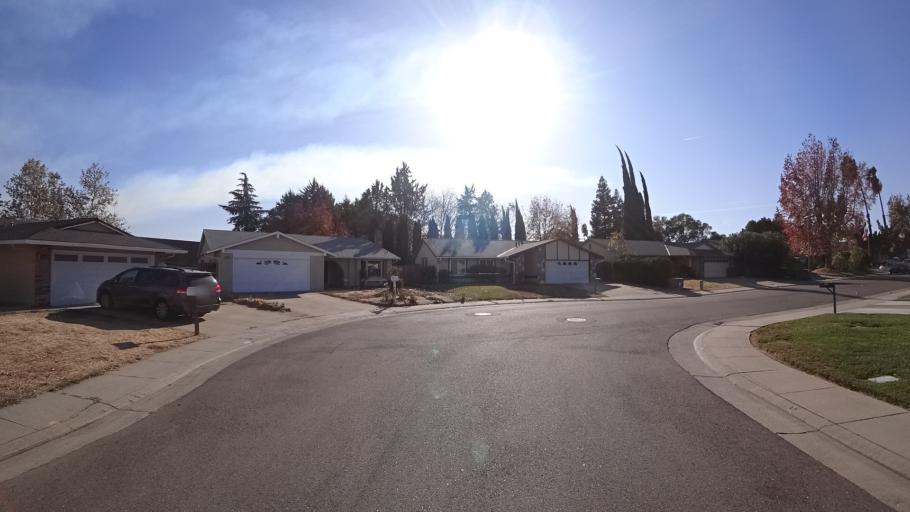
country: US
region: California
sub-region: Sacramento County
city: Antelope
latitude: 38.6979
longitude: -121.3218
